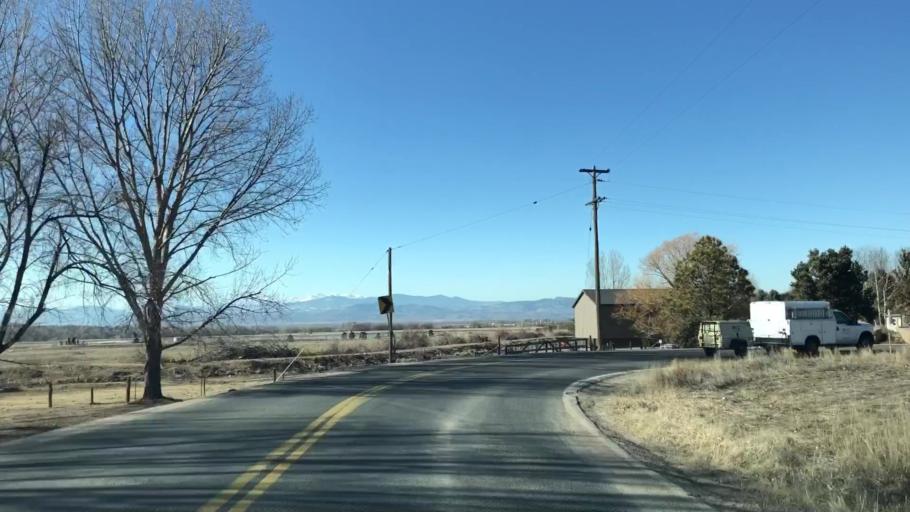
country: US
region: Colorado
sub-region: Weld County
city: Windsor
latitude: 40.4901
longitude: -104.9437
